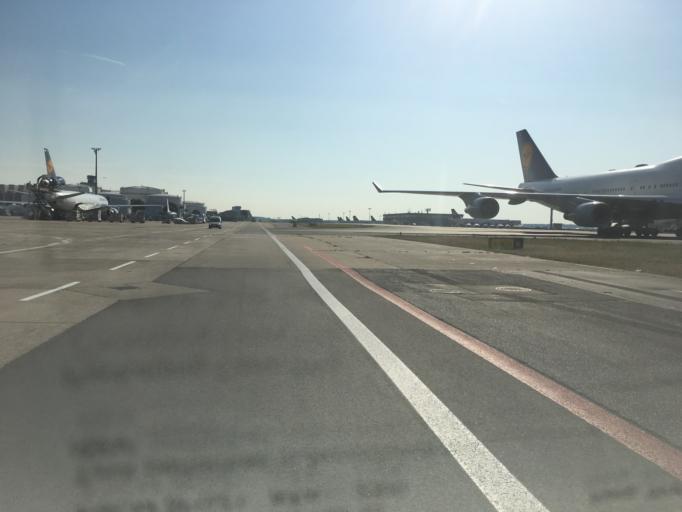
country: DE
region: Hesse
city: Kelsterbach
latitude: 50.0396
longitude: 8.5455
